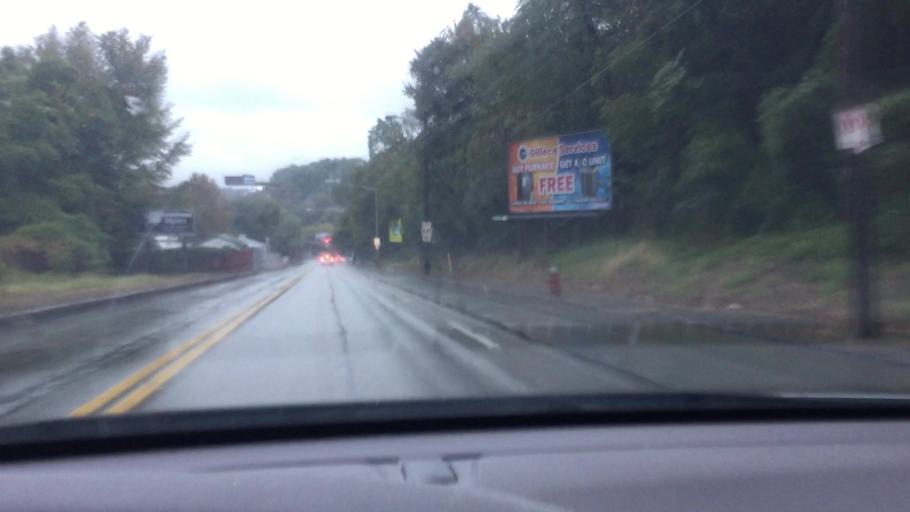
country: US
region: Pennsylvania
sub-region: Allegheny County
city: Mount Oliver
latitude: 40.4226
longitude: -79.9505
